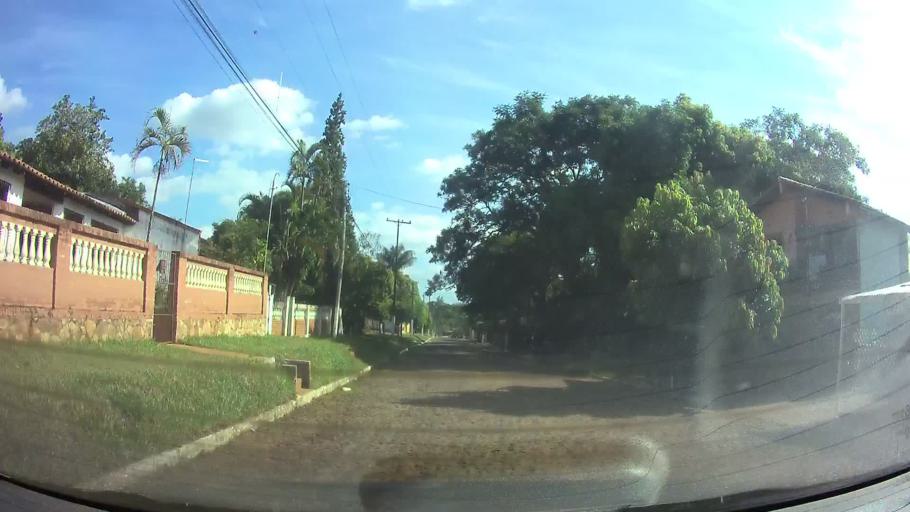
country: PY
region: Central
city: Limpio
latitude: -25.2512
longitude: -57.4706
